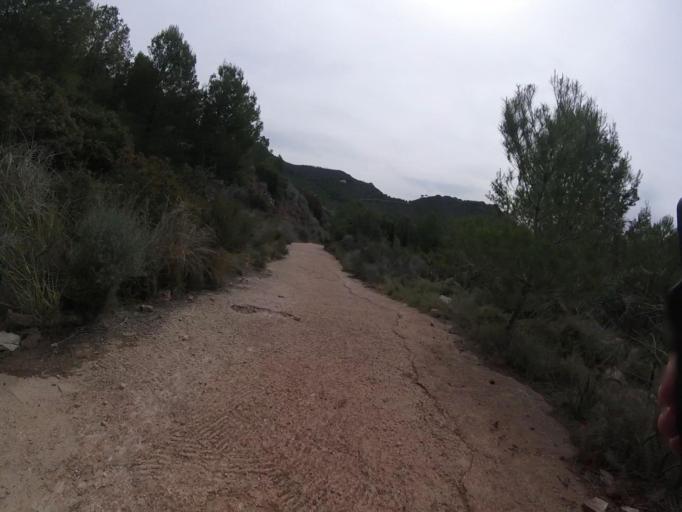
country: ES
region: Valencia
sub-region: Provincia de Castello
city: Benicassim
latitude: 40.0762
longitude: 0.0356
